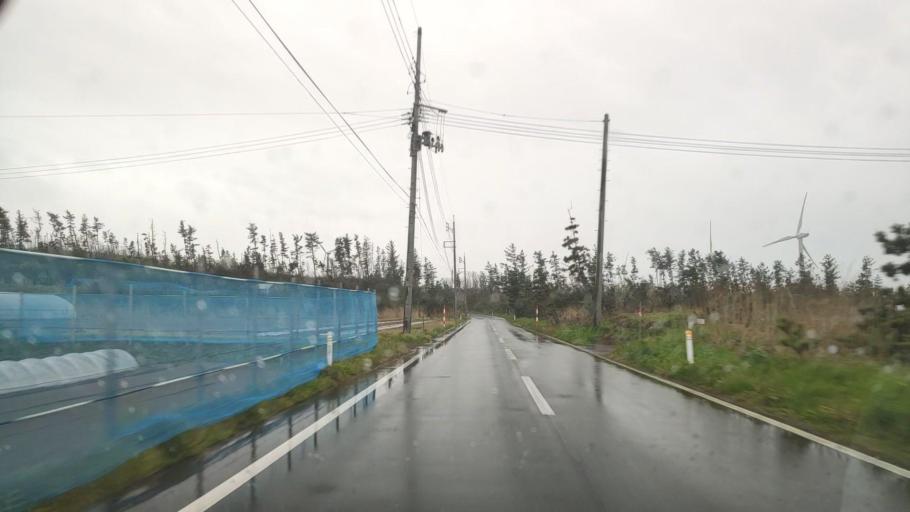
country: JP
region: Akita
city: Noshiromachi
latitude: 40.0817
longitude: 139.9553
